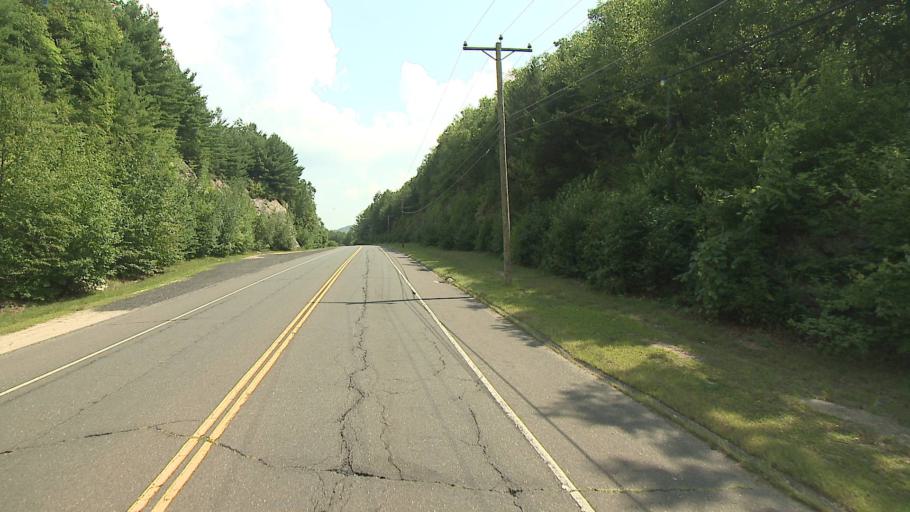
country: US
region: Connecticut
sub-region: Litchfield County
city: Thomaston
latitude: 41.6612
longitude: -73.1076
